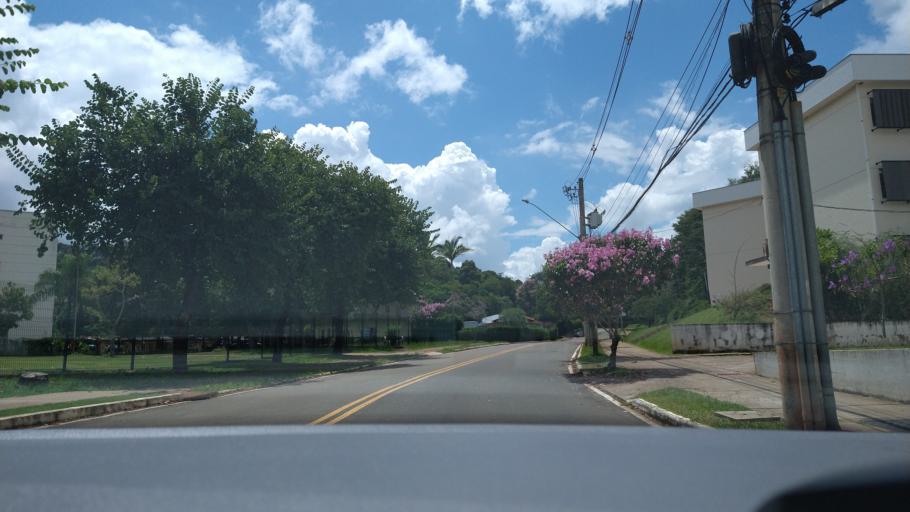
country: BR
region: Minas Gerais
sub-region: Vicosa
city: Vicosa
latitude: -20.7614
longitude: -42.8644
